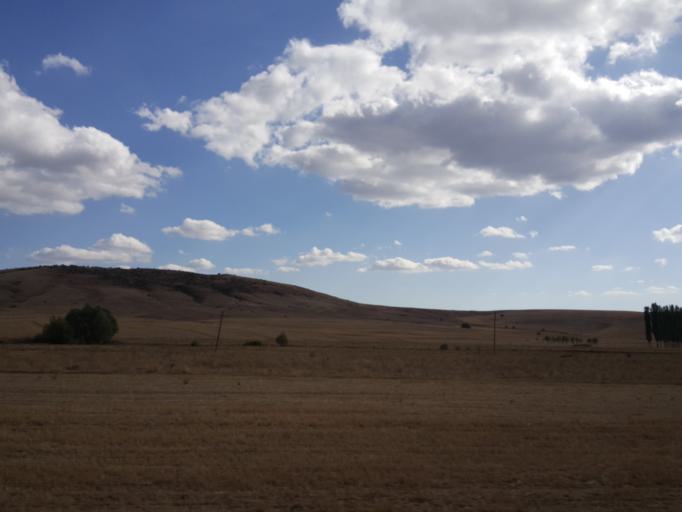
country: TR
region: Tokat
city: Sulusaray
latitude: 39.9862
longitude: 35.9499
